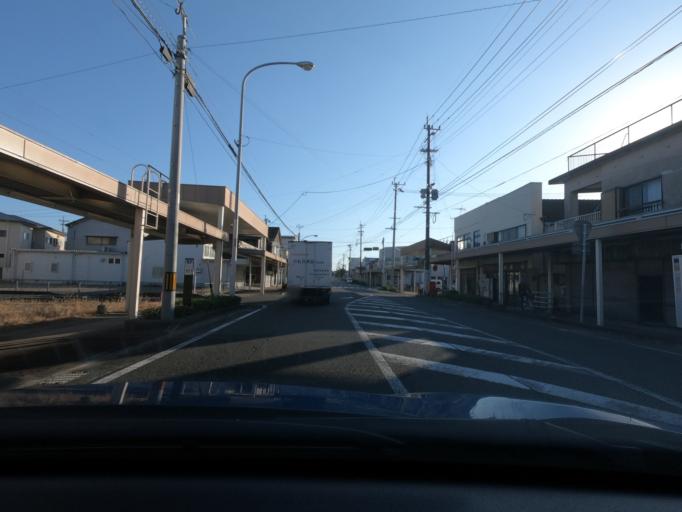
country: JP
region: Kagoshima
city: Akune
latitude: 32.0141
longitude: 130.1962
